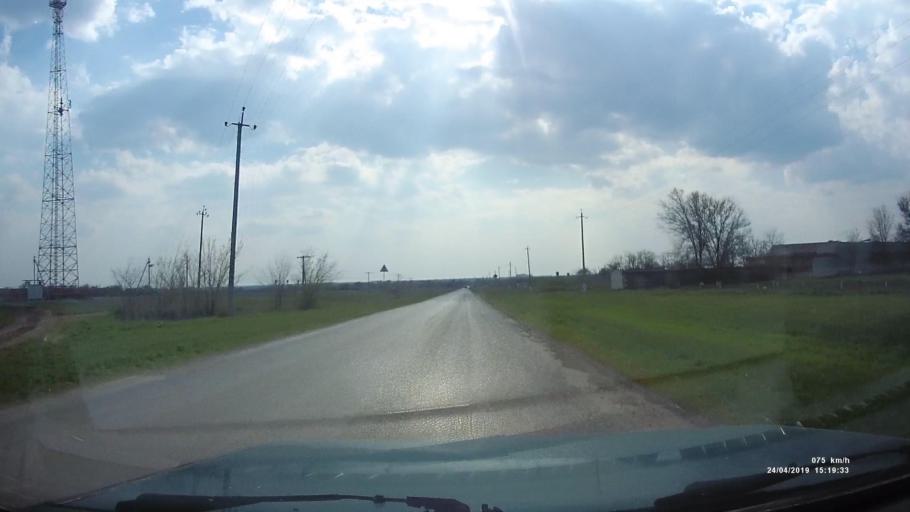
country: RU
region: Rostov
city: Remontnoye
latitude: 46.5393
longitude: 43.1442
